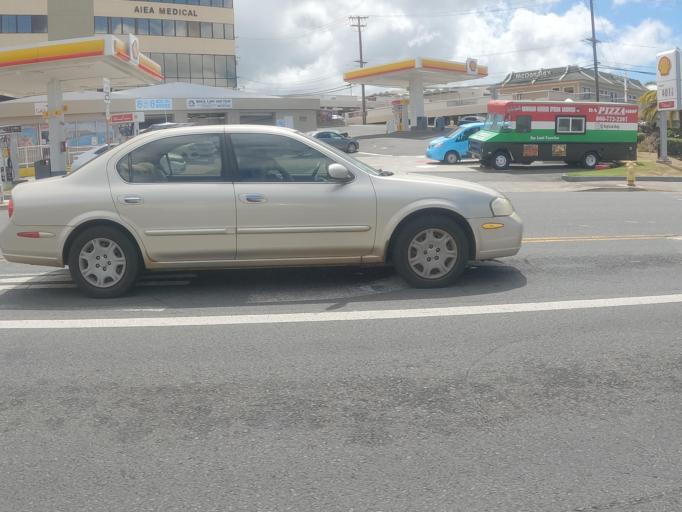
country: US
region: Hawaii
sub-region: Honolulu County
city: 'Aiea
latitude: 21.3793
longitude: -157.9310
